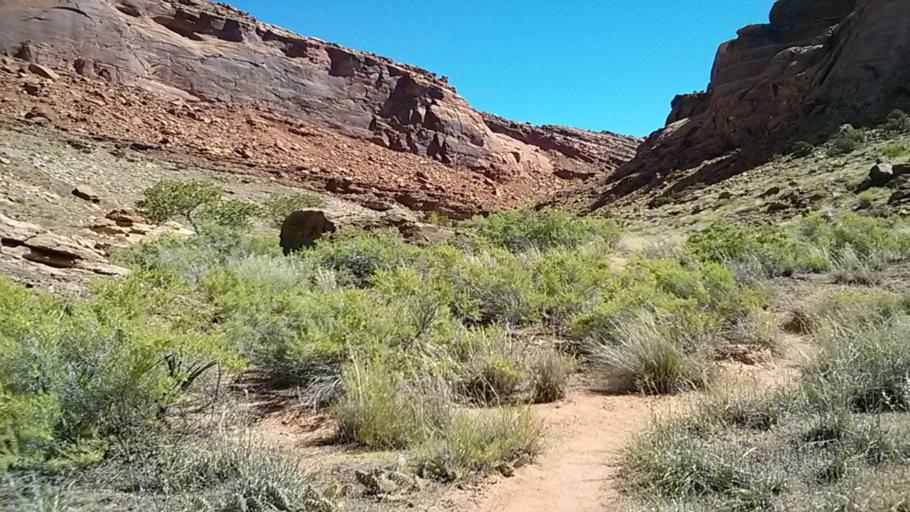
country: US
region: Utah
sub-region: Grand County
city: Moab
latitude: 38.4464
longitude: -109.9514
